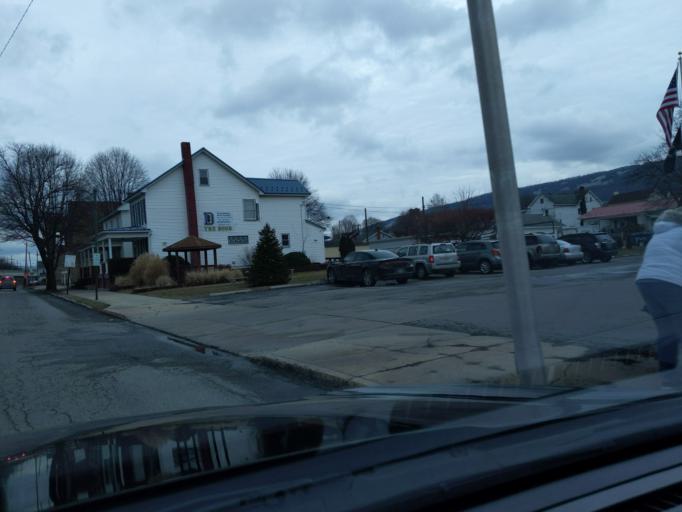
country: US
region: Pennsylvania
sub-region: Blair County
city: Bellwood
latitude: 40.6007
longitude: -78.3327
